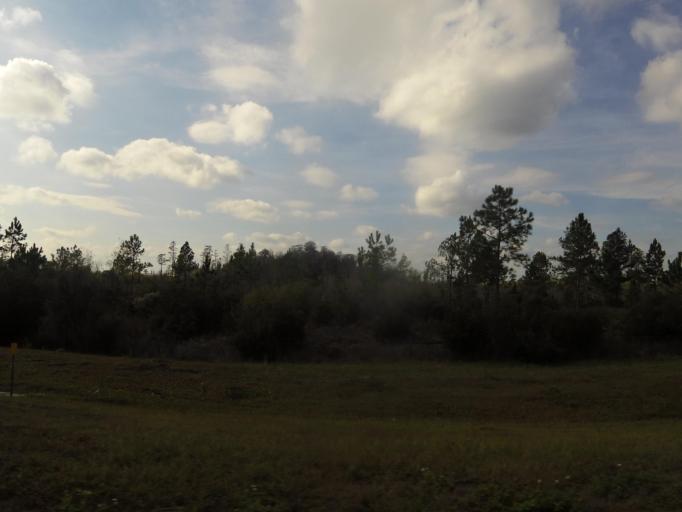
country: US
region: Florida
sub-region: Duval County
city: Baldwin
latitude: 30.2778
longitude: -81.8776
